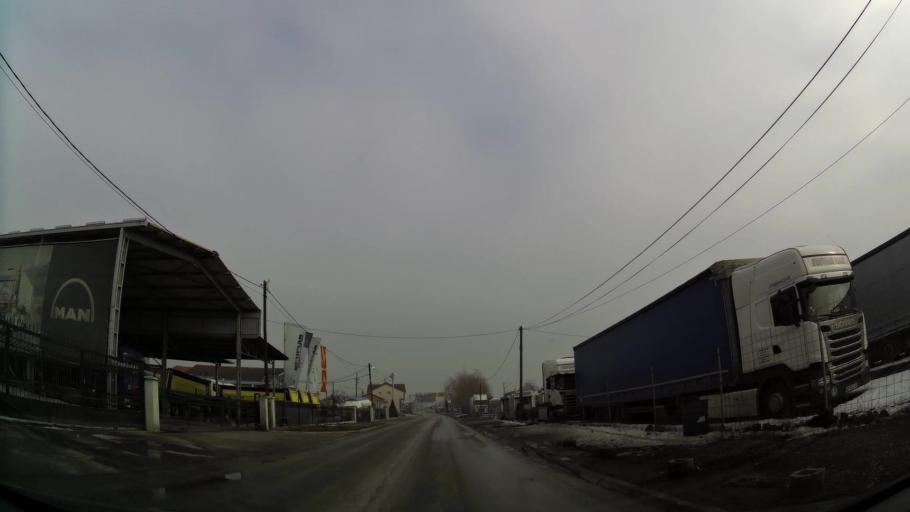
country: MK
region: Ilinden
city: Ilinden
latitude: 41.9951
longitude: 21.5542
